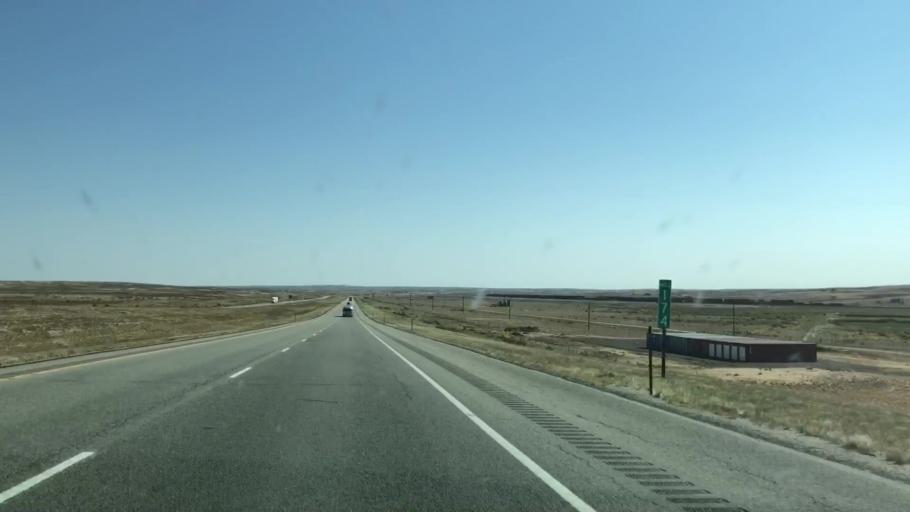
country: US
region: Wyoming
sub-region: Carbon County
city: Rawlins
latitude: 41.6787
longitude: -107.9708
